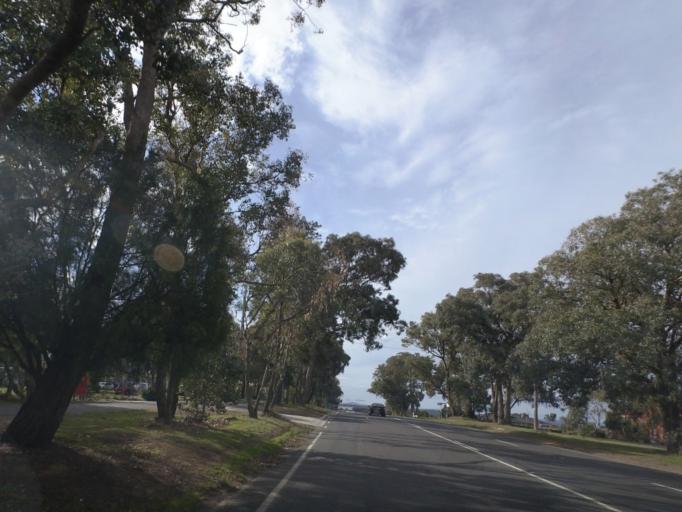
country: AU
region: Victoria
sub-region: Manningham
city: Donvale
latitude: -37.7667
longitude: 145.1718
